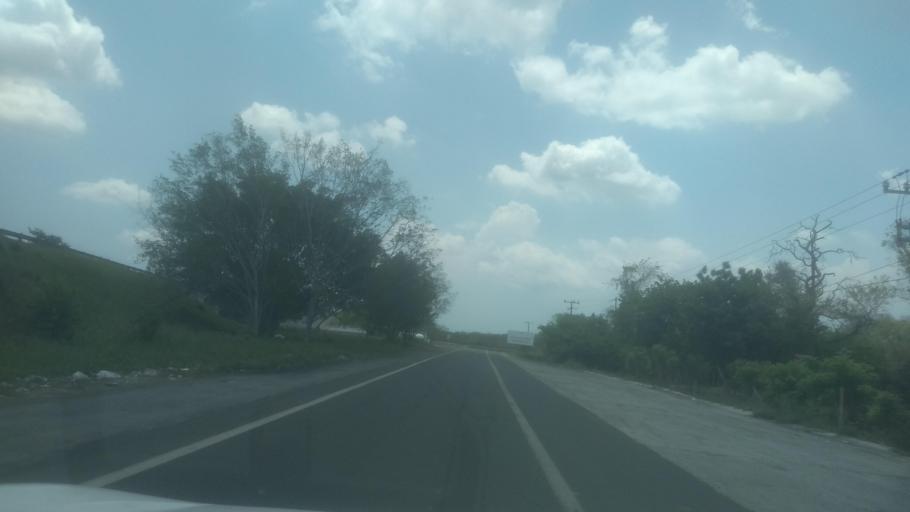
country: MX
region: Veracruz
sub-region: Emiliano Zapata
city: Plan del Rio
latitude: 19.3930
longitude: -96.6151
